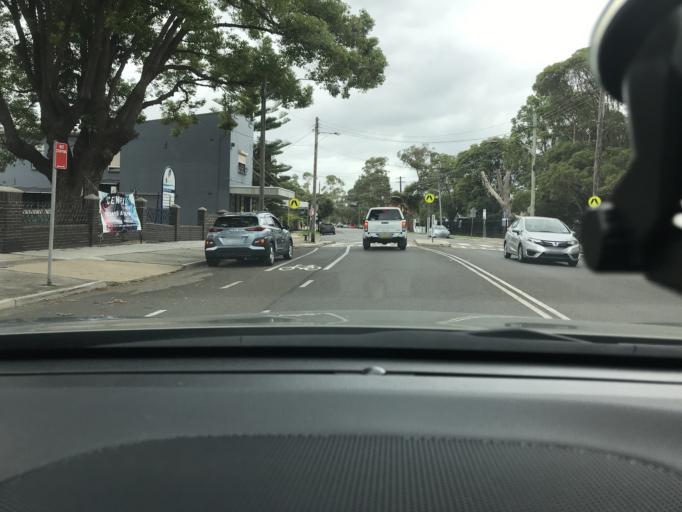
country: AU
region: New South Wales
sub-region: Canada Bay
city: Wareemba
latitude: -33.8537
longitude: 151.1299
